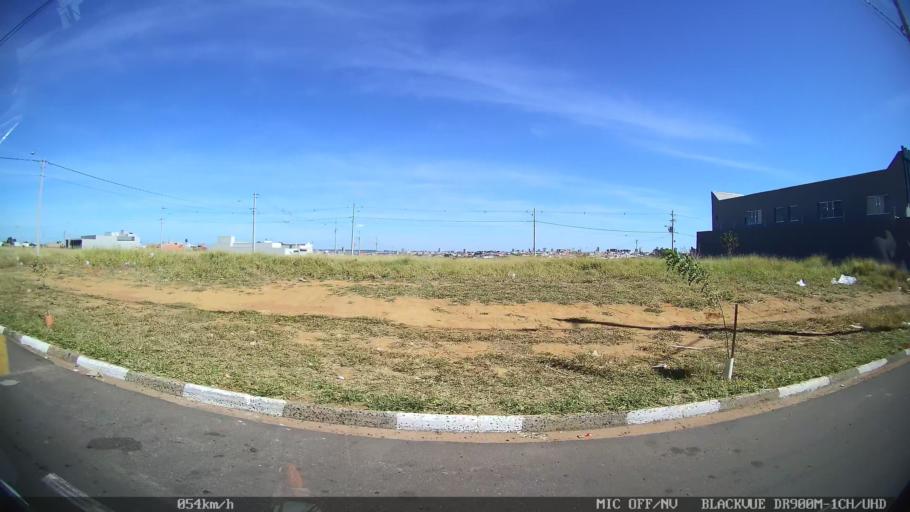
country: BR
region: Sao Paulo
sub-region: Franca
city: Franca
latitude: -20.5495
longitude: -47.3602
